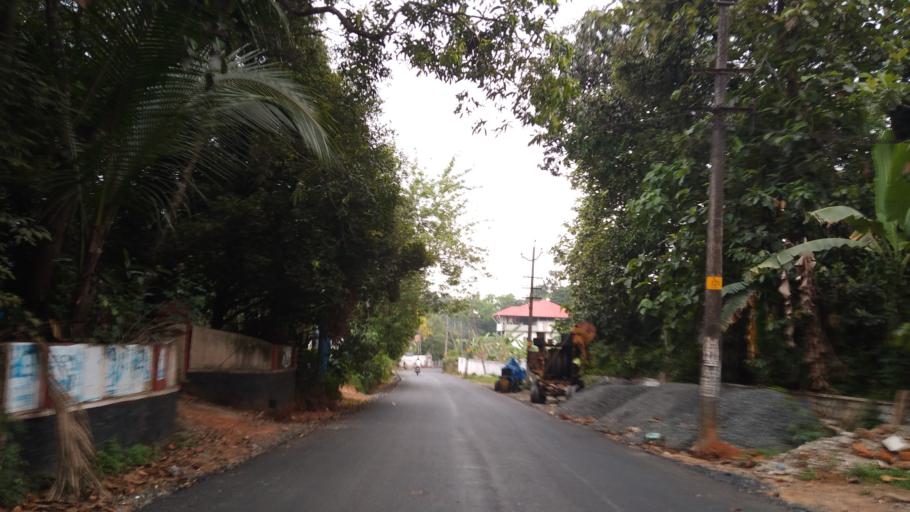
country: IN
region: Kerala
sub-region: Ernakulam
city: Perumbavoor
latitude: 10.0671
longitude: 76.5040
